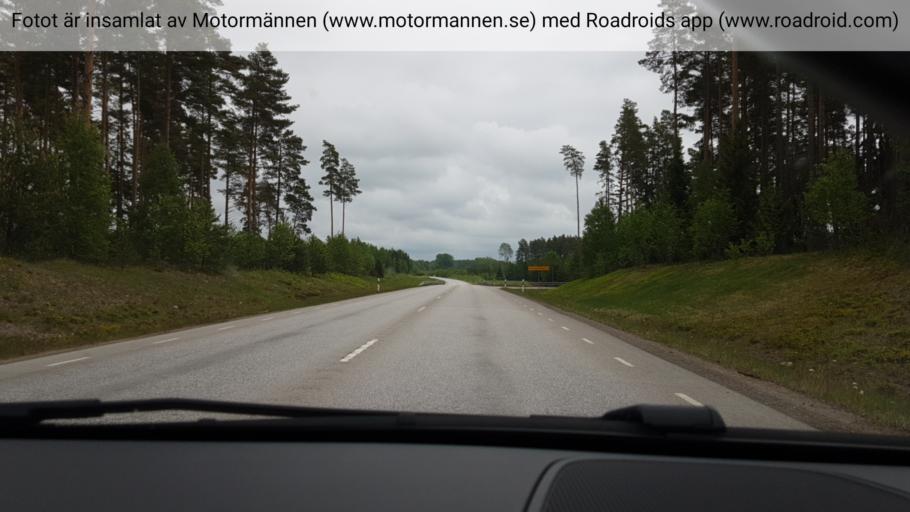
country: SE
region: Uppsala
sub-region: Osthammars Kommun
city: Bjorklinge
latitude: 60.0091
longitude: 17.6005
